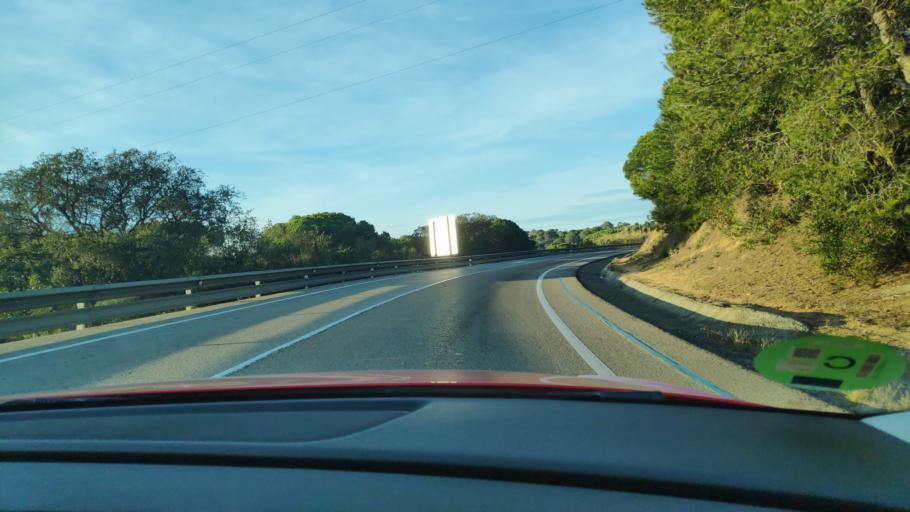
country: ES
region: Catalonia
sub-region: Provincia de Girona
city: Lloret de Mar
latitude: 41.7187
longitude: 2.8259
